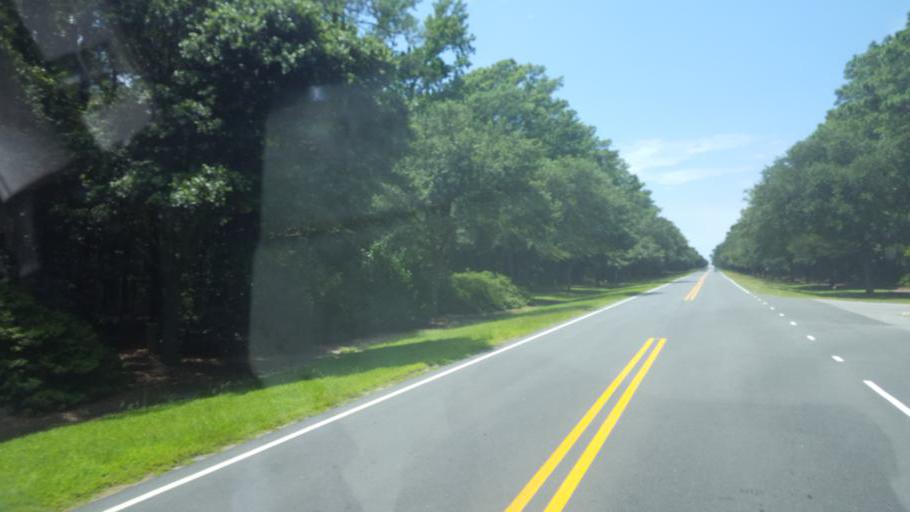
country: US
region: North Carolina
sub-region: Dare County
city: Manteo
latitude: 35.9305
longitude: -75.7138
